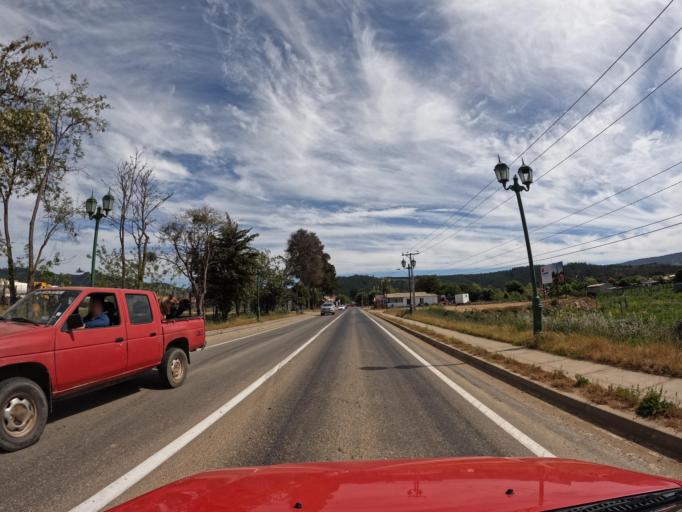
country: CL
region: Maule
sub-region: Provincia de Talca
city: Constitucion
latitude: -35.0880
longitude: -72.0201
